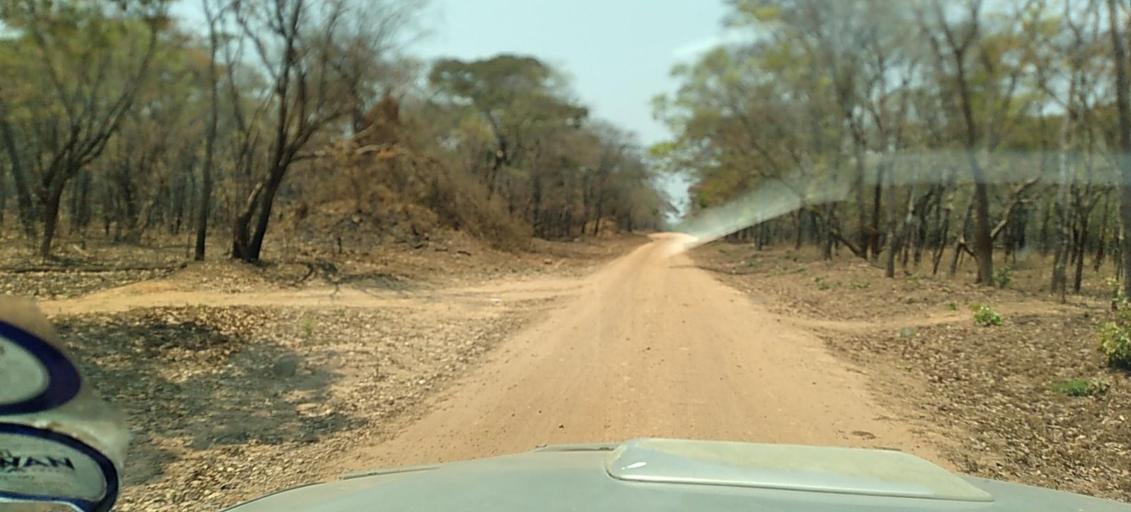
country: ZM
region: North-Western
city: Kasempa
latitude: -13.5573
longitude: 26.0751
